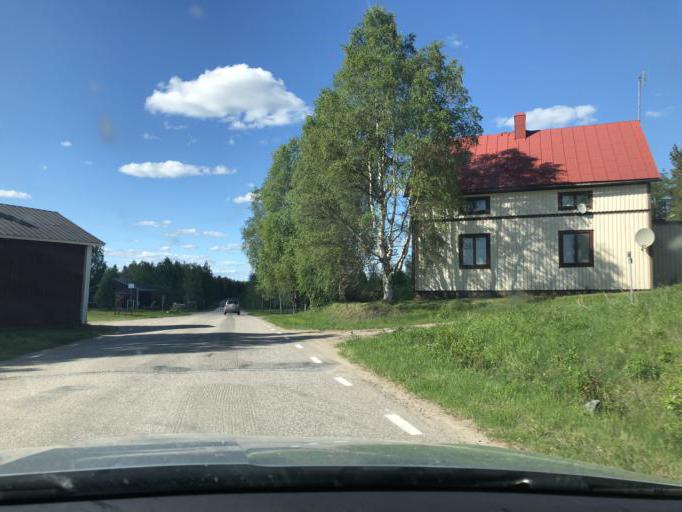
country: SE
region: Norrbotten
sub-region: Kalix Kommun
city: Kalix
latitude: 65.9260
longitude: 23.1642
